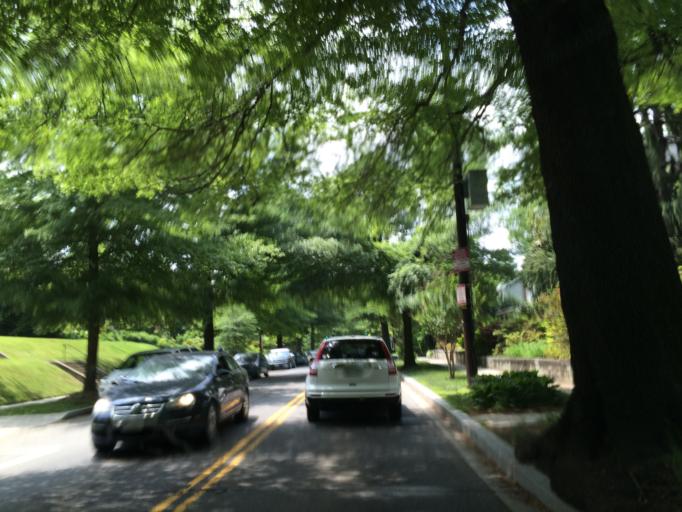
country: US
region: Maryland
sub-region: Montgomery County
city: Chevy Chase Village
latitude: 38.9610
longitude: -77.0755
